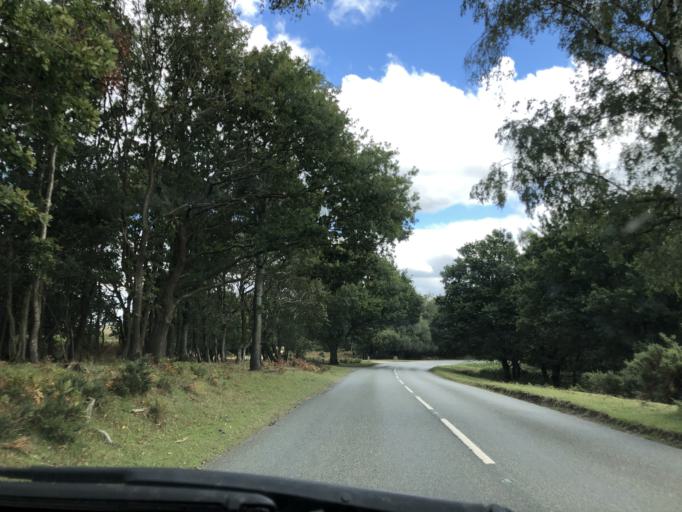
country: GB
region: England
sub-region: East Sussex
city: Uckfield
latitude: 51.0398
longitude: 0.0799
